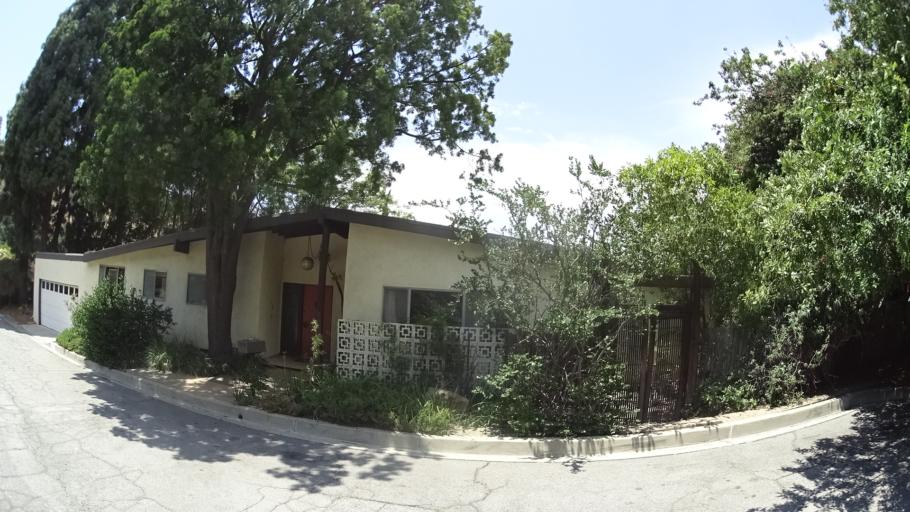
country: US
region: California
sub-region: Los Angeles County
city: Sherman Oaks
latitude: 34.1364
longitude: -118.4301
